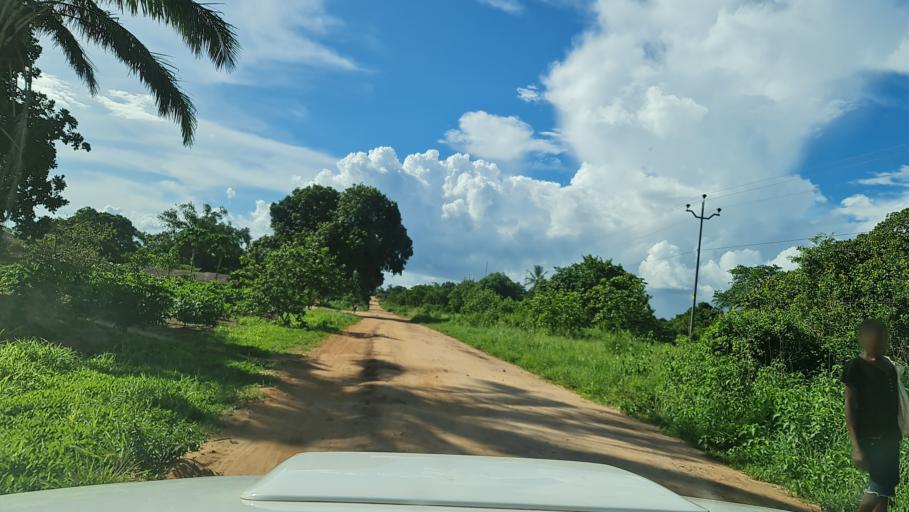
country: MZ
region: Nampula
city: Ilha de Mocambique
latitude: -15.2938
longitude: 40.1200
